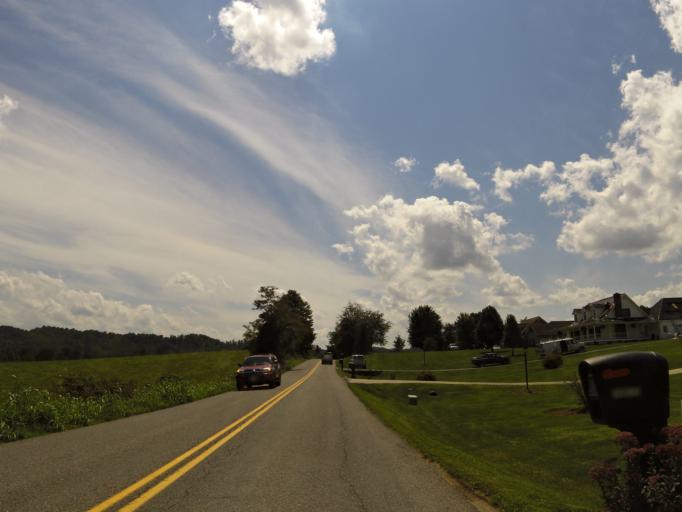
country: US
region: Virginia
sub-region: Washington County
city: Abingdon
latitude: 36.6835
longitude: -81.9284
